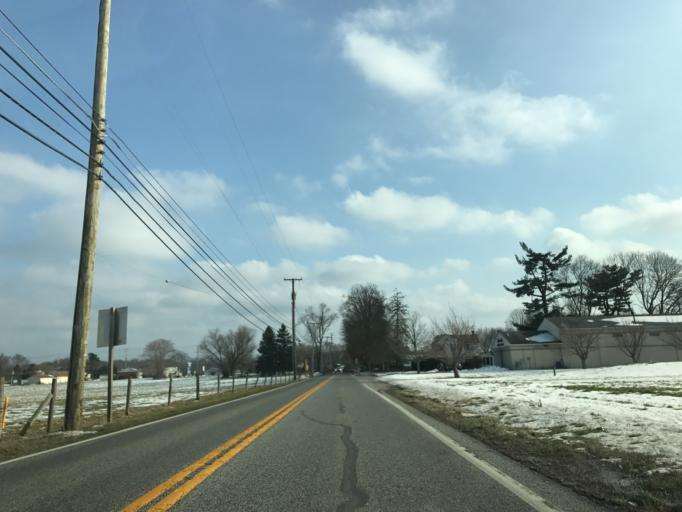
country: US
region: Maryland
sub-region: Harford County
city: Bel Air South
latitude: 39.5620
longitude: -76.2528
